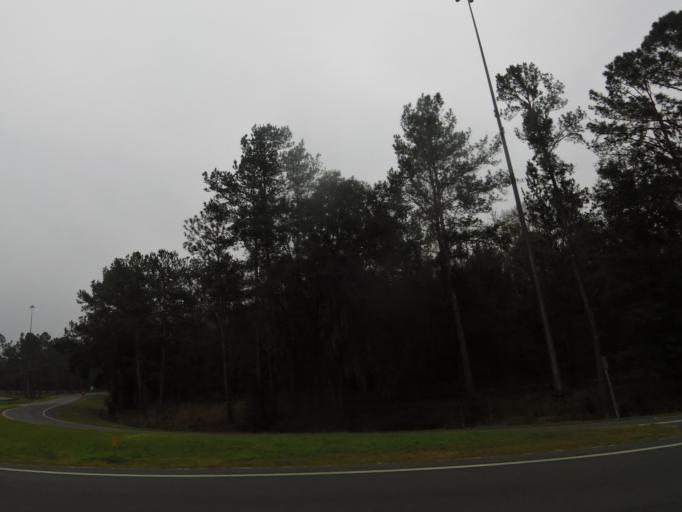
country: US
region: Florida
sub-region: Alachua County
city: High Springs
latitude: 29.8721
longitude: -82.5452
